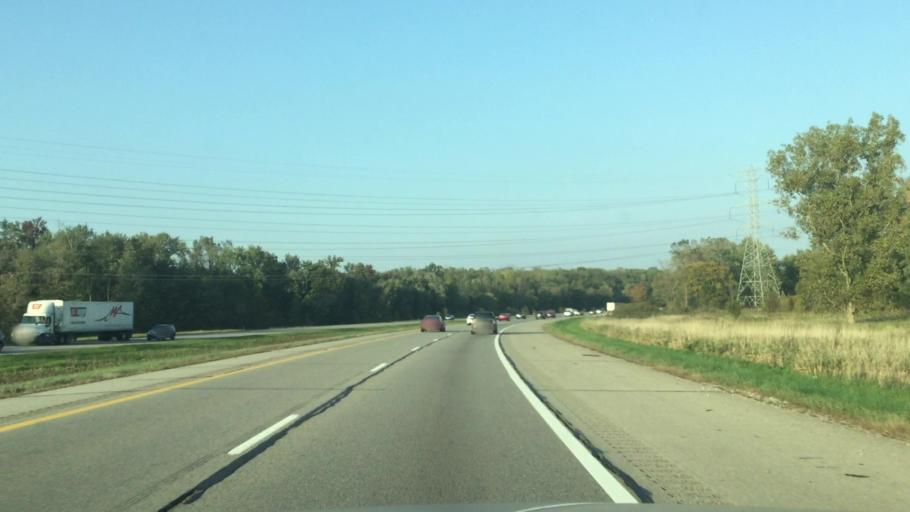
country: US
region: Michigan
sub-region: Washtenaw County
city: Ypsilanti
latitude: 42.3537
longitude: -83.5897
